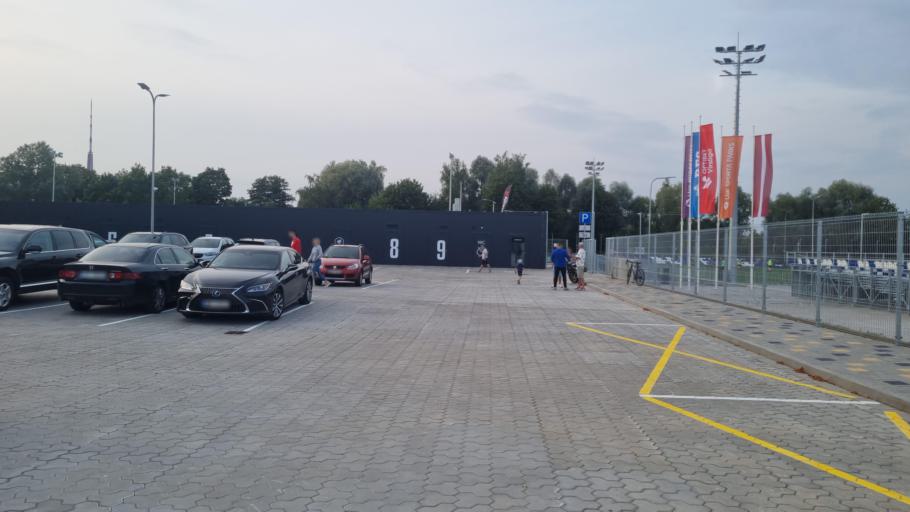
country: LV
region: Kekava
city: Balozi
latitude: 56.9080
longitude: 24.1542
